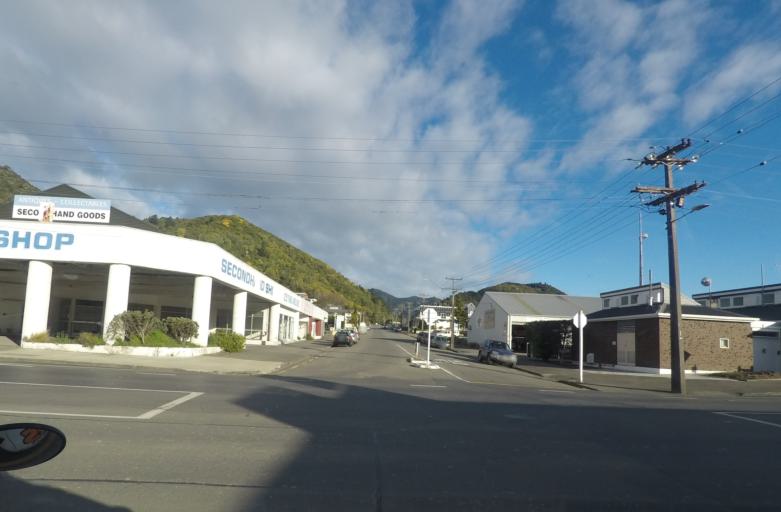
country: NZ
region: Marlborough
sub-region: Marlborough District
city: Picton
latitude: -41.2905
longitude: 174.0080
